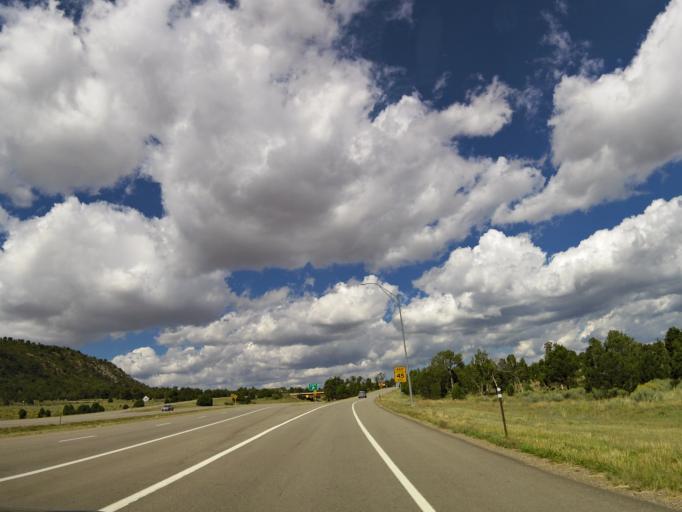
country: US
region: Colorado
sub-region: Montezuma County
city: Mancos
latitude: 37.3397
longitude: -108.4071
